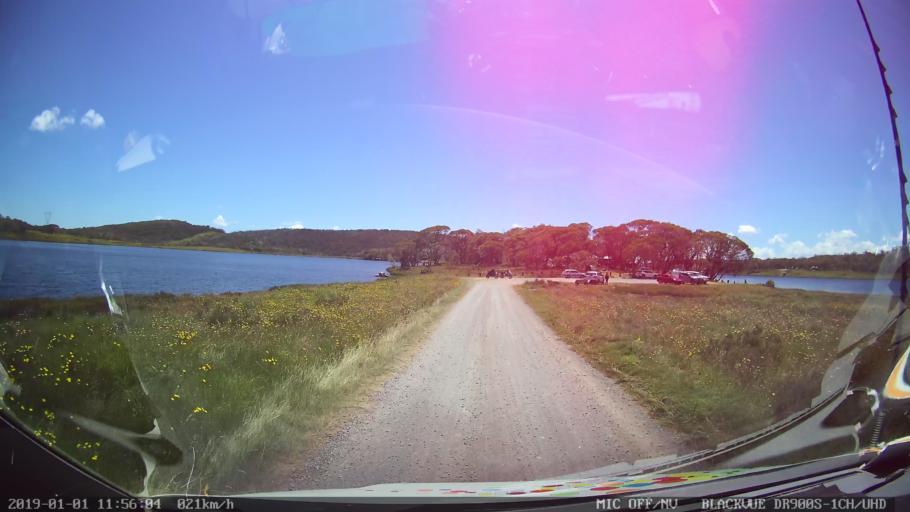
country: AU
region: New South Wales
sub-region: Snowy River
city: Jindabyne
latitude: -35.8867
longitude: 148.4501
